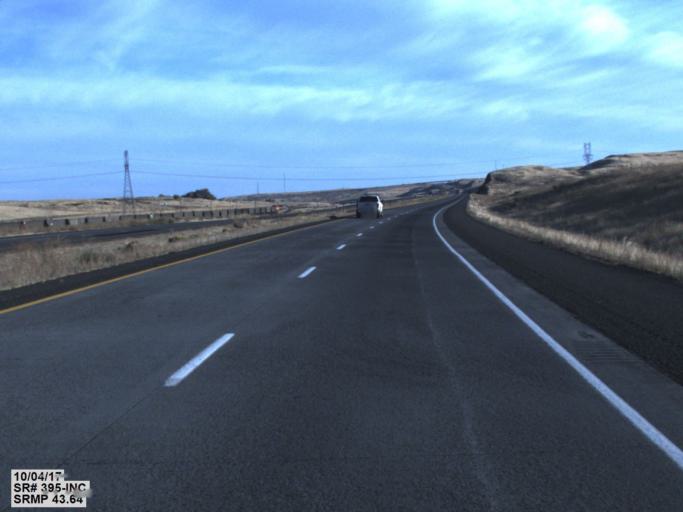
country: US
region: Washington
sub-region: Franklin County
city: Basin City
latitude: 46.5377
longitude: -119.0128
